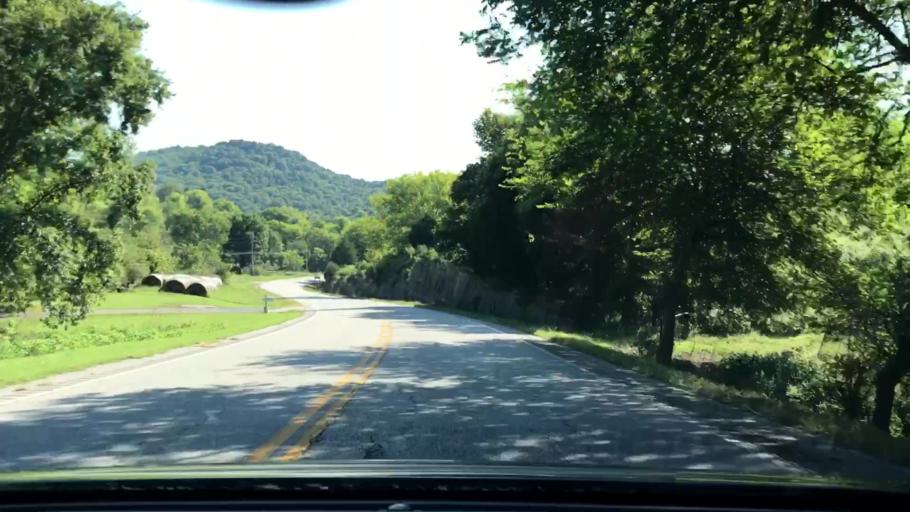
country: US
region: Tennessee
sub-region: Jackson County
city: Gainesboro
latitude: 36.3643
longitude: -85.7619
